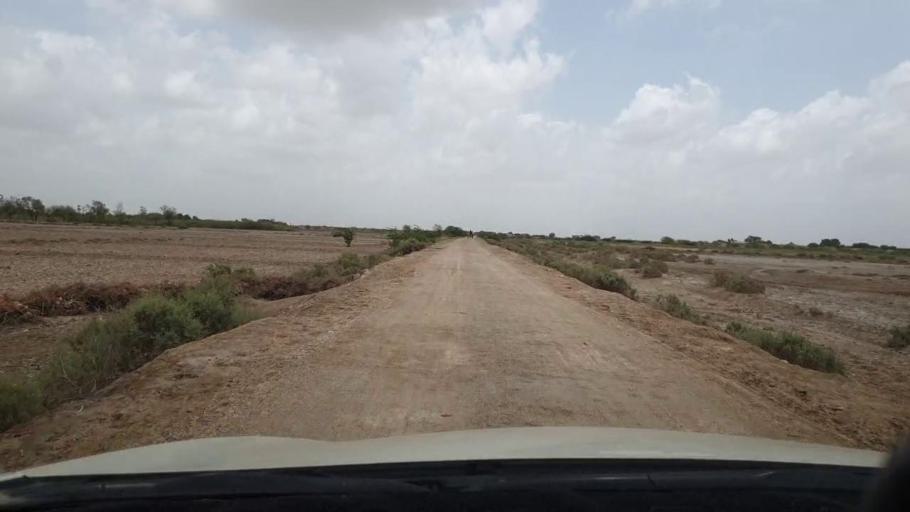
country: PK
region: Sindh
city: Kadhan
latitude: 24.3603
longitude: 68.9335
